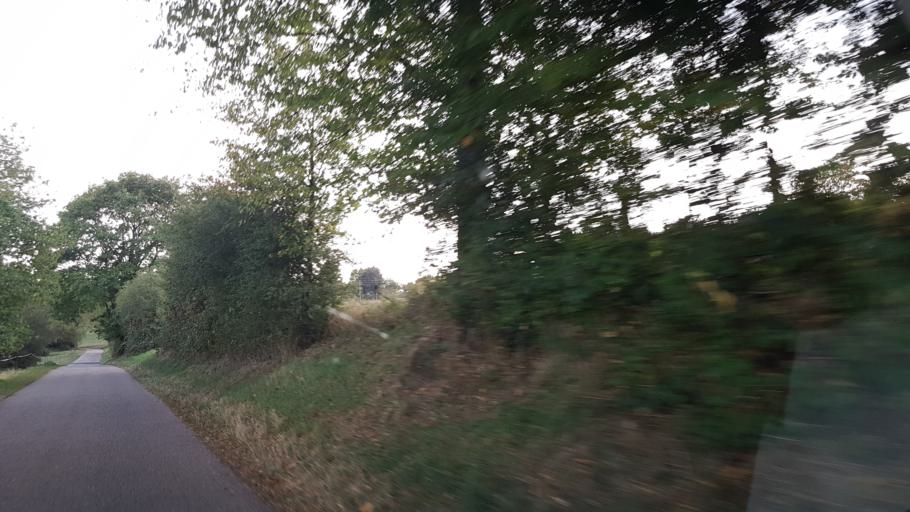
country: DE
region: Saarland
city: Eppelborn
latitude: 49.3986
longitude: 7.0063
